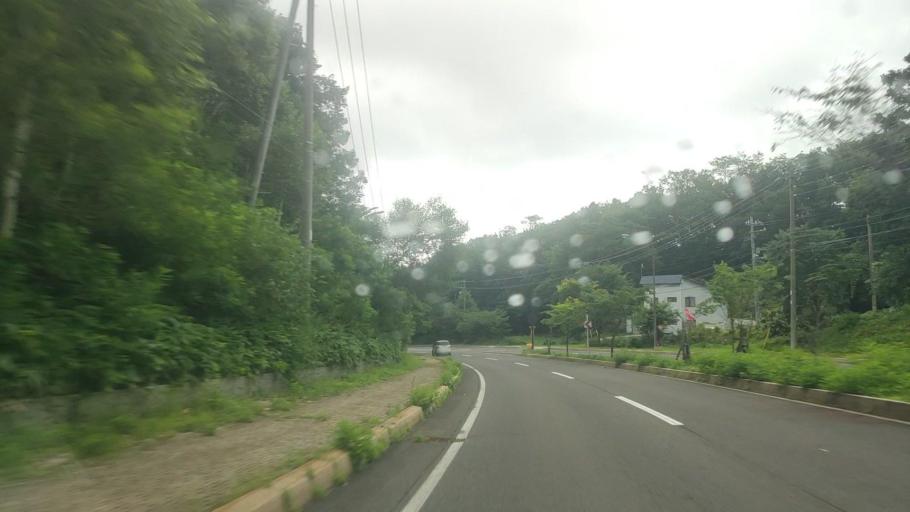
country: JP
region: Hokkaido
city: Shiraoi
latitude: 42.4705
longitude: 141.1489
